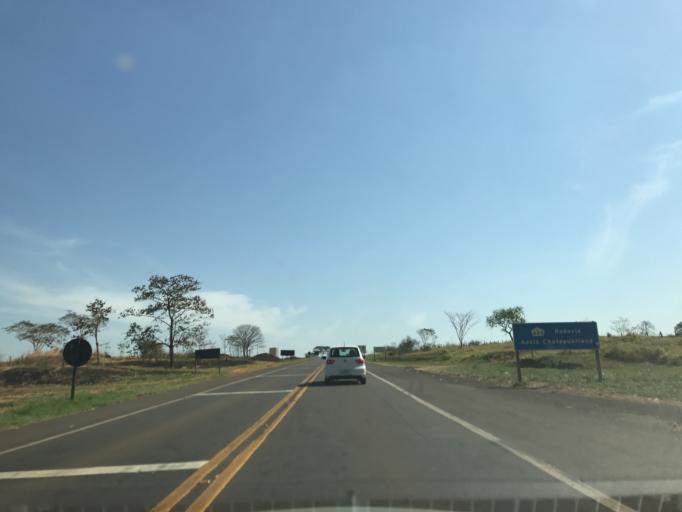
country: BR
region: Sao Paulo
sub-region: Jose Bonifacio
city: Jose Bonifacio
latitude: -21.0431
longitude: -49.7011
